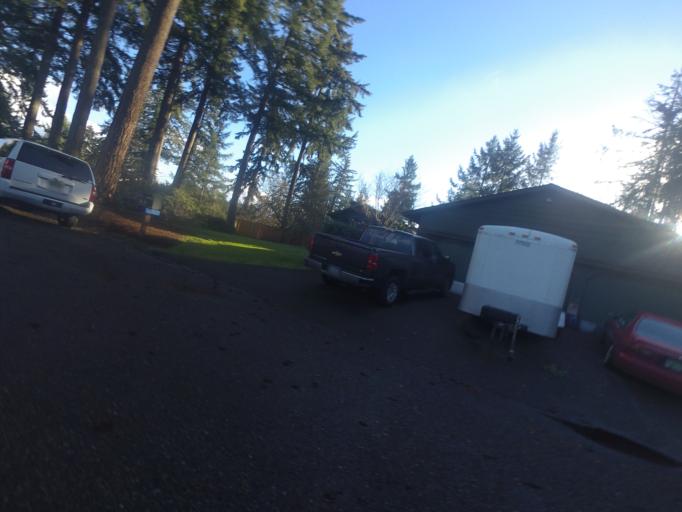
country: US
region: Washington
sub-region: Pierce County
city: Fircrest
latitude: 47.2268
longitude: -122.5307
